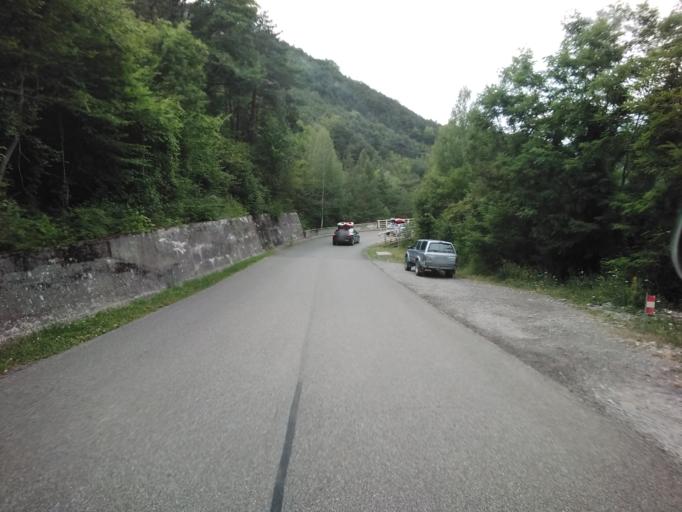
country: FR
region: Provence-Alpes-Cote d'Azur
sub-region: Departement des Alpes-de-Haute-Provence
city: Seyne-les-Alpes
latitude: 44.4523
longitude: 6.3871
